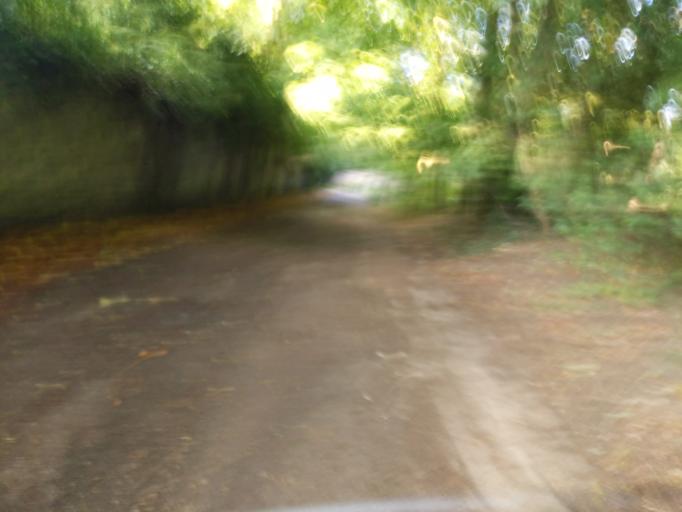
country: FR
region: Ile-de-France
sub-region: Departement des Yvelines
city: Saint-Remy-les-Chevreuse
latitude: 48.7022
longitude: 2.0897
